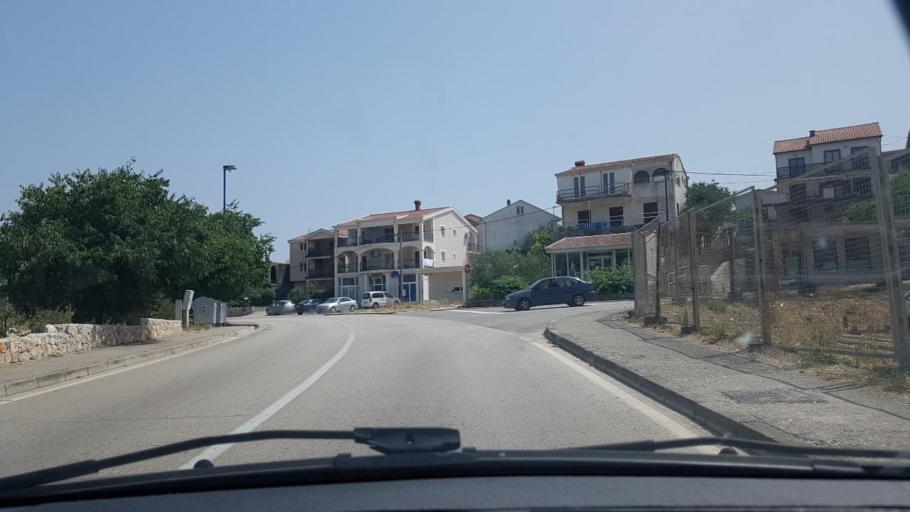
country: BA
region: Federation of Bosnia and Herzegovina
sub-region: Hercegovacko-Bosanski Kanton
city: Neum
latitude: 42.9254
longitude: 17.6207
